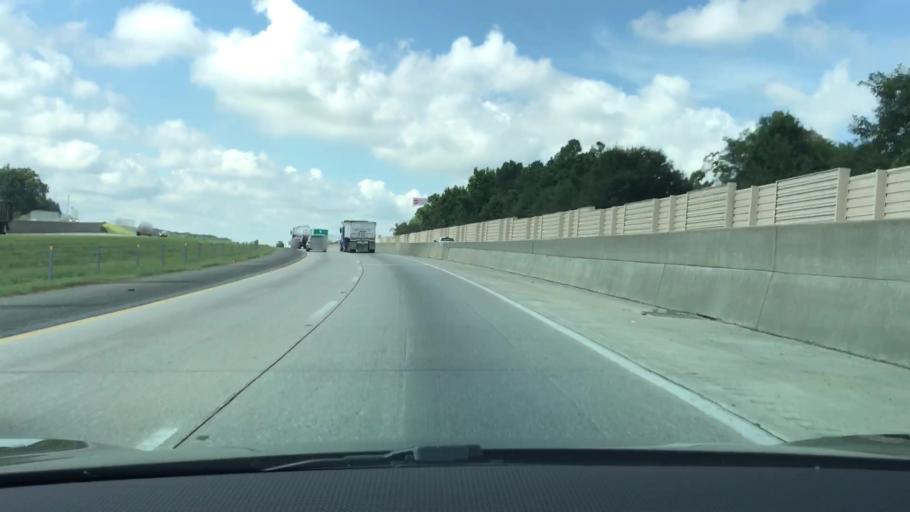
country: US
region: Georgia
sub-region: Hall County
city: Oakwood
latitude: 34.2299
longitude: -83.8593
